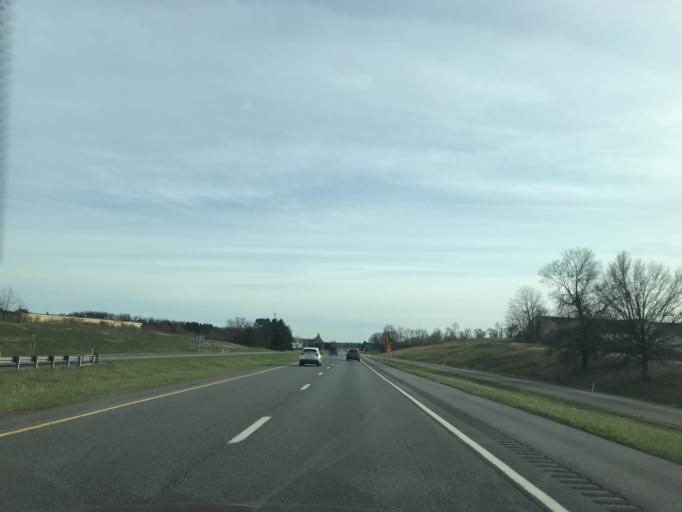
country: US
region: Pennsylvania
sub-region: Northumberland County
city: Watsontown
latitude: 41.0611
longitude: -76.8357
